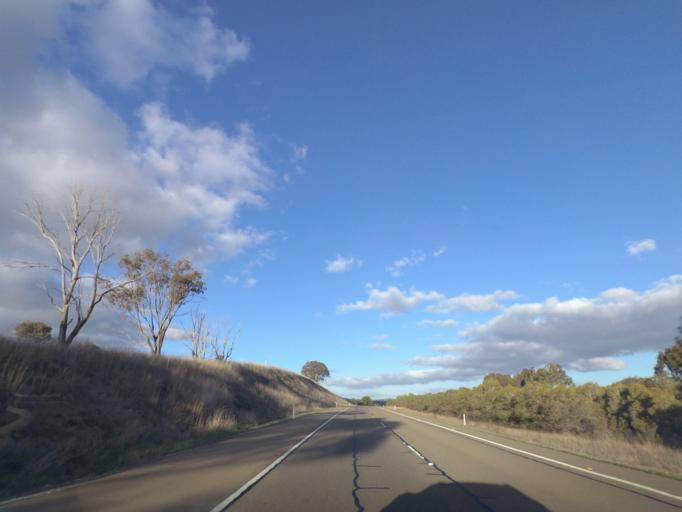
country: AU
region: New South Wales
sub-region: Yass Valley
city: Yass
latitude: -34.8076
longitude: 148.5884
